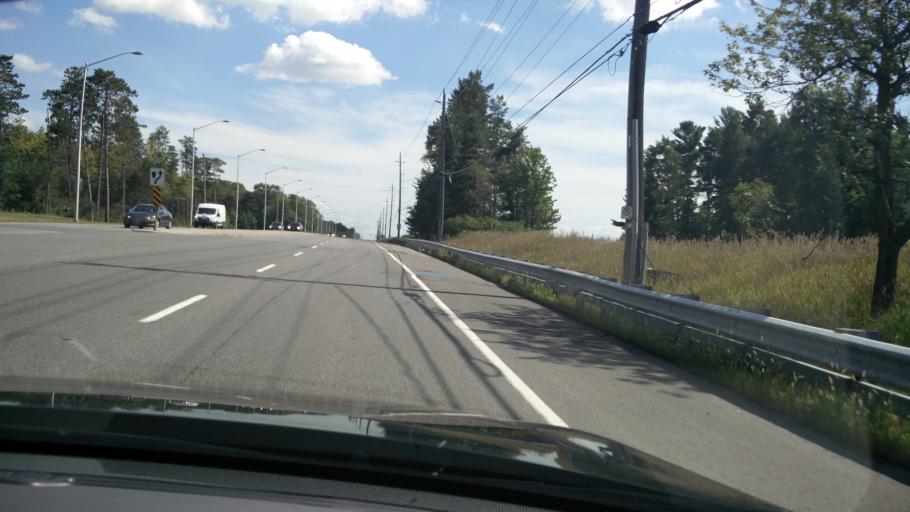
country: CA
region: Ontario
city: Bells Corners
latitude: 45.3228
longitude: -75.7453
